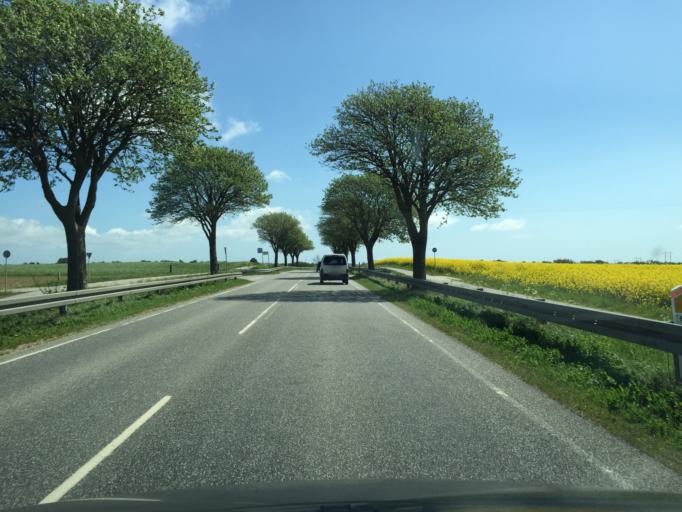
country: DK
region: Zealand
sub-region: Vordingborg Kommune
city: Stege
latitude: 54.9818
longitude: 12.1761
